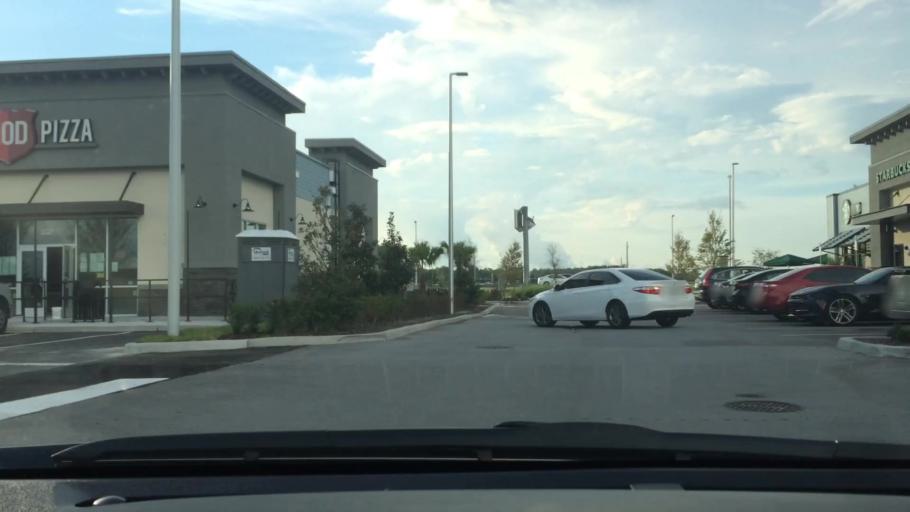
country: US
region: Florida
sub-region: Hillsborough County
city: Pebble Creek
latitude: 28.1907
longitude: -82.3952
